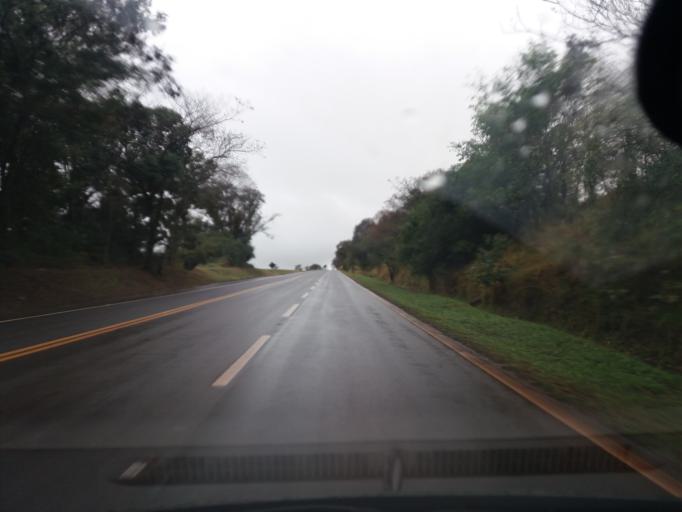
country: BR
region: Parana
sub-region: Campo Mourao
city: Campo Mourao
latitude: -24.3197
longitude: -52.6370
